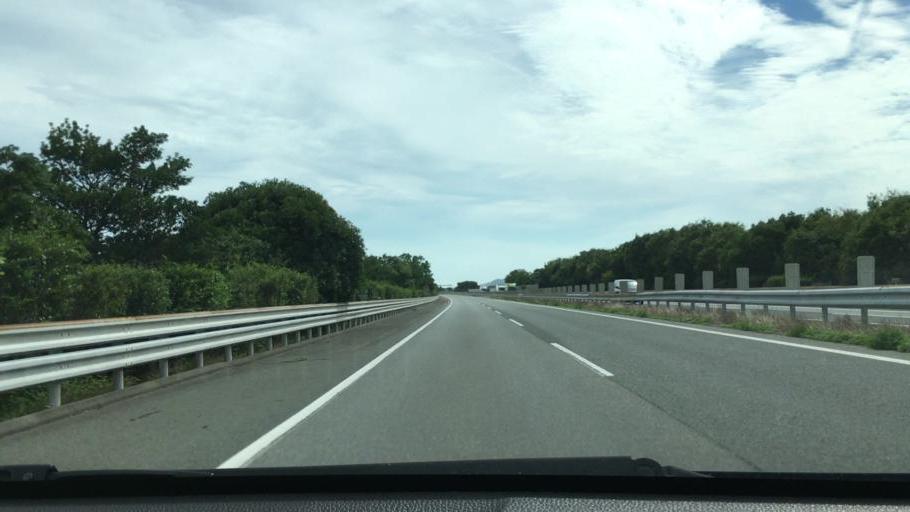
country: JP
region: Yamaguchi
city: Hofu
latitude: 34.0638
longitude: 131.5487
